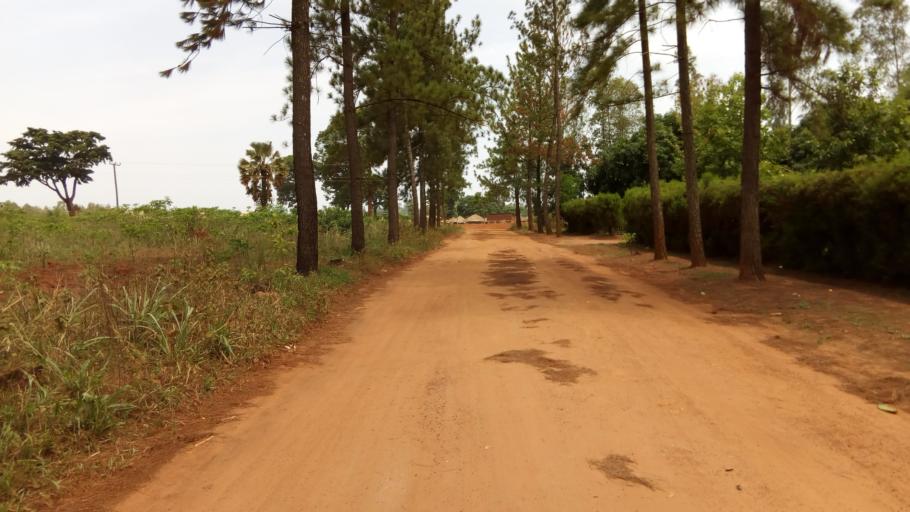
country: UG
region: Northern Region
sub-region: Gulu District
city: Gulu
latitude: 2.7732
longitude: 32.3191
